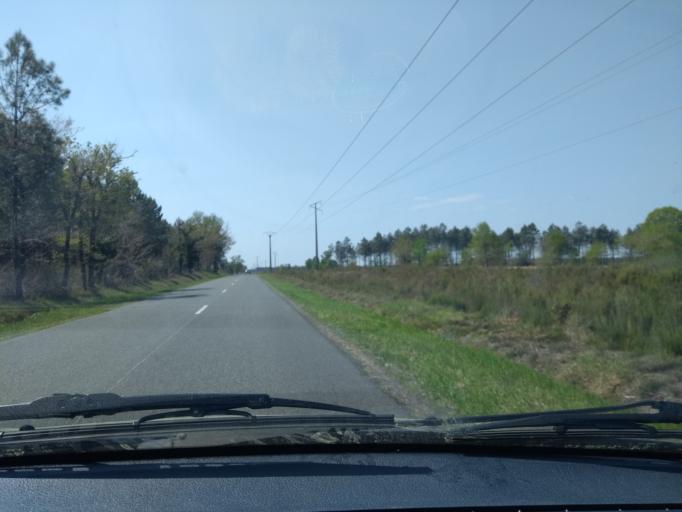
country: FR
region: Aquitaine
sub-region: Departement de la Gironde
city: Belin-Beliet
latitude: 44.5280
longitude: -0.6934
